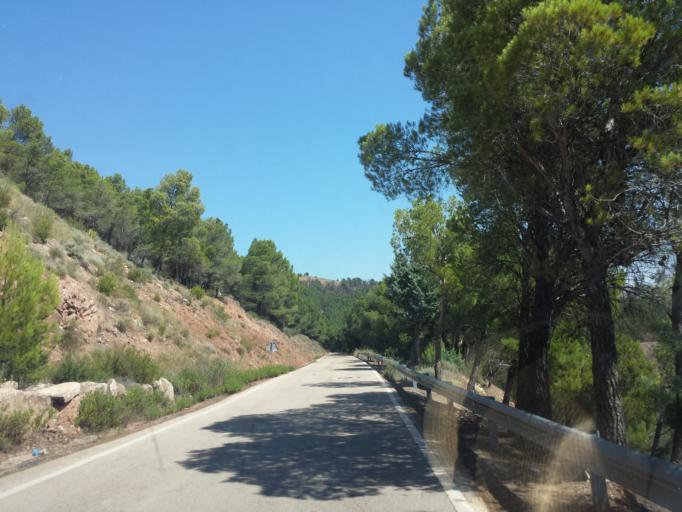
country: ES
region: Aragon
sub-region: Provincia de Zaragoza
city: Carenas
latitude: 41.2522
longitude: -1.8080
